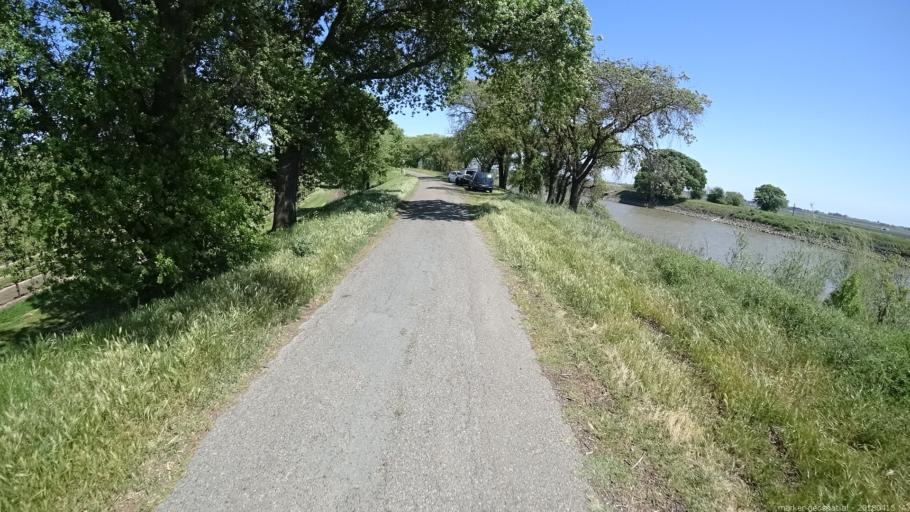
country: US
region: California
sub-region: Sacramento County
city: Walnut Grove
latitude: 38.2550
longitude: -121.5985
